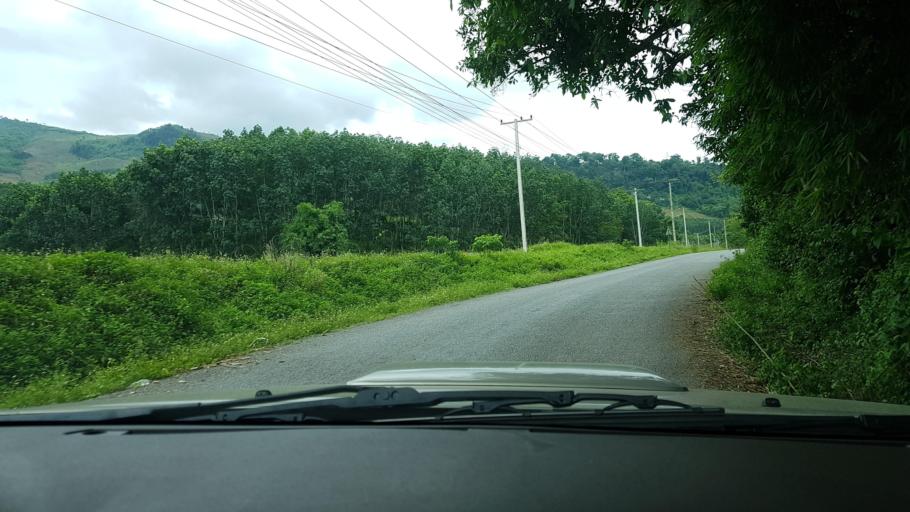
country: LA
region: Loungnamtha
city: Muang Nale
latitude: 20.1851
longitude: 101.5196
